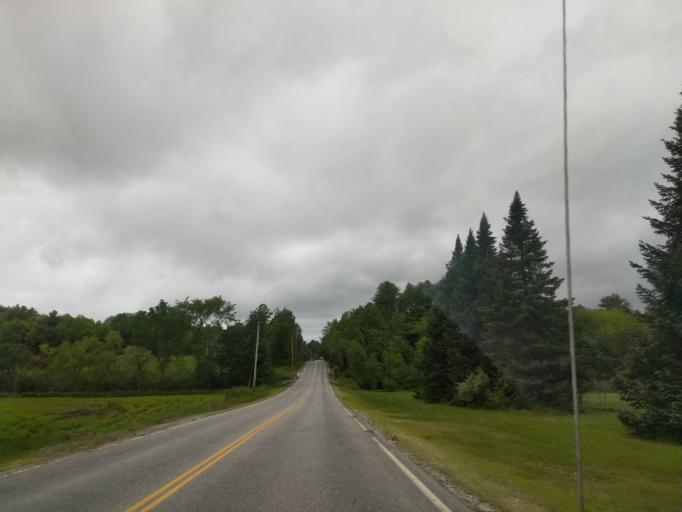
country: US
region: Maine
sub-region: Cumberland County
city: North Windham
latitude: 43.8277
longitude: -70.3938
